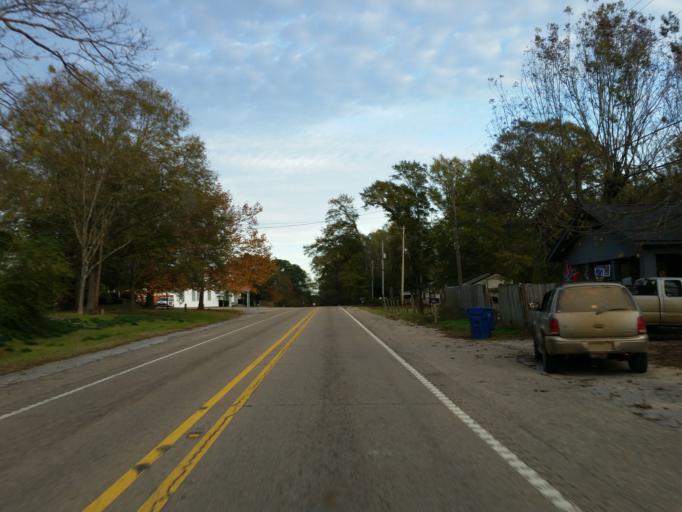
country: US
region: Mississippi
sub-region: Lauderdale County
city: Marion
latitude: 32.4184
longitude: -88.5055
